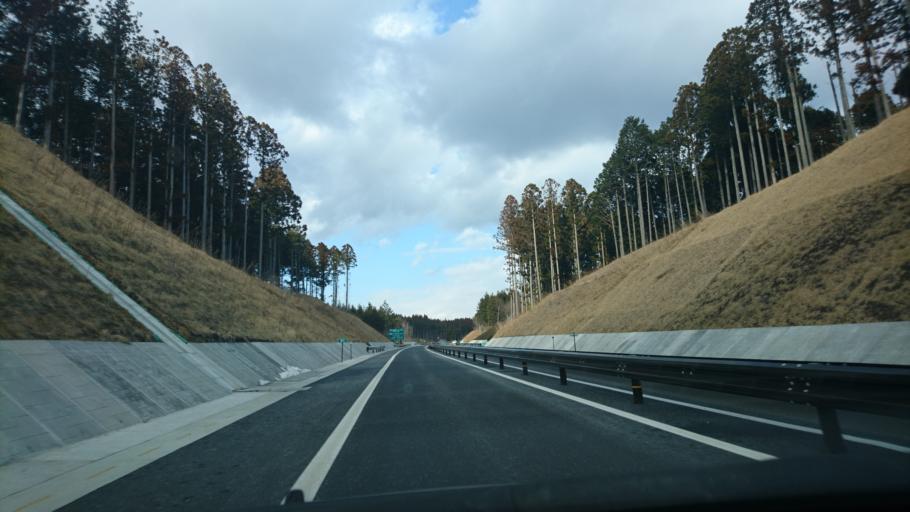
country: JP
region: Miyagi
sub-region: Oshika Gun
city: Onagawa Cho
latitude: 38.7209
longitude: 141.5118
